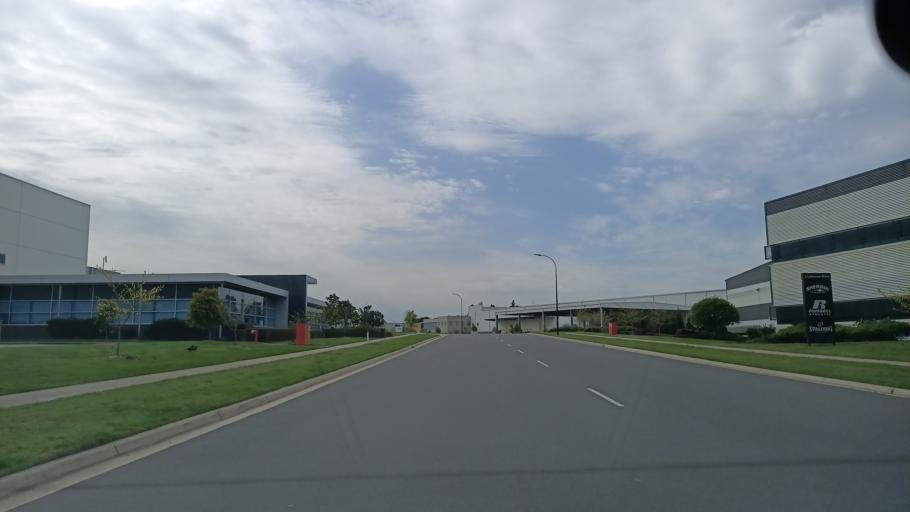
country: AU
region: Victoria
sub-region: Knox
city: Scoresby
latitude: -37.9083
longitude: 145.2219
